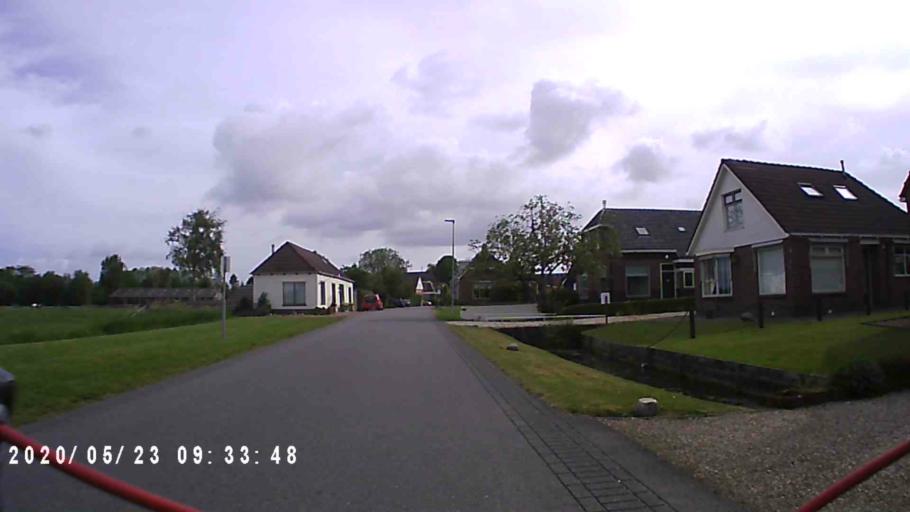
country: NL
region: Groningen
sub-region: Gemeente Slochteren
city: Slochteren
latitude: 53.3007
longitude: 6.7239
